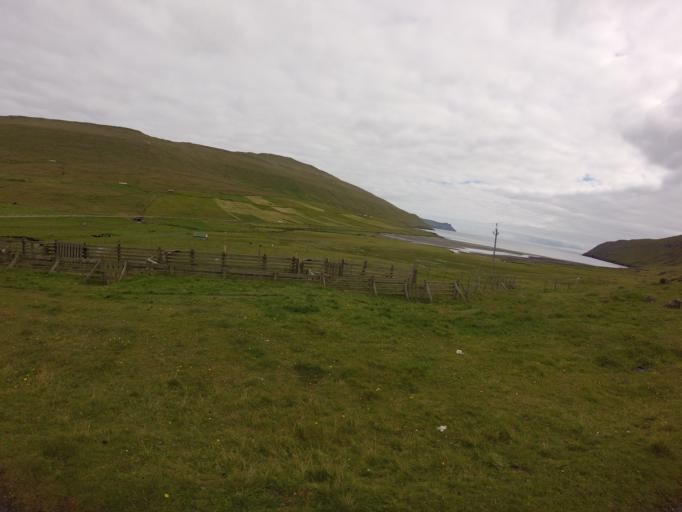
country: FO
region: Suduroy
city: Tvoroyri
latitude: 61.6254
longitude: -6.9424
